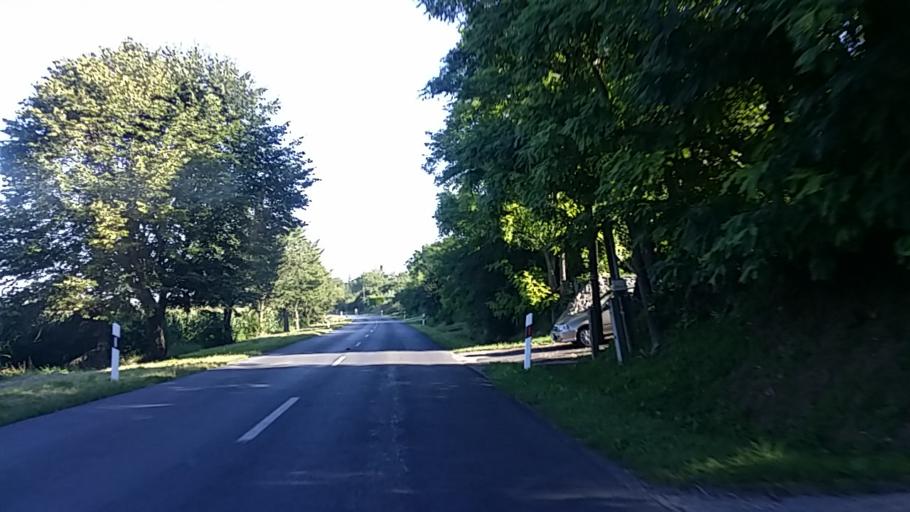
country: HU
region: Zala
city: Cserszegtomaj
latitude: 46.8225
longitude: 17.2018
